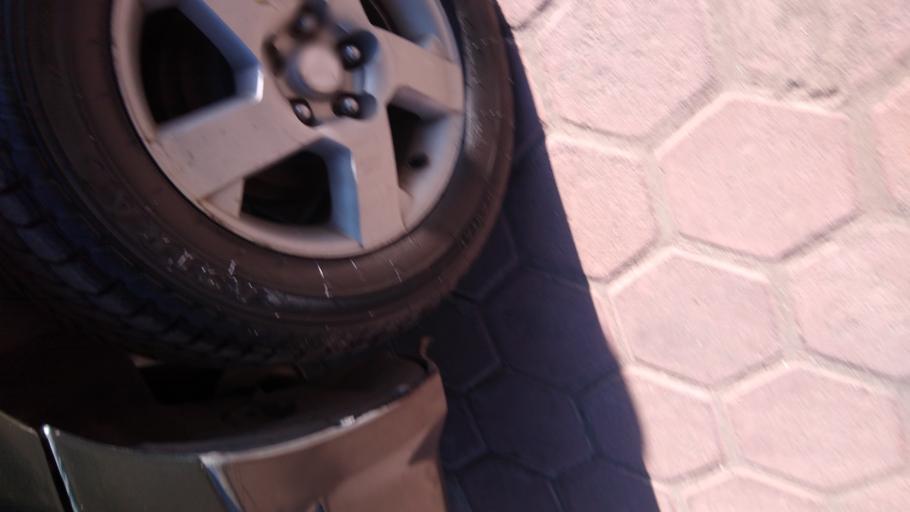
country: MX
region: Puebla
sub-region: San Pedro Cholula
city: Santiago Momoxpan
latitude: 19.0585
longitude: -98.2734
